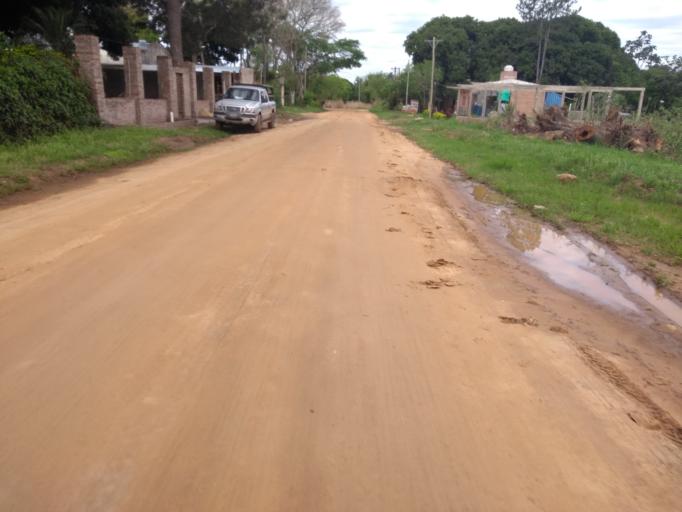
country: AR
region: Corrientes
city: San Luis del Palmar
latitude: -27.4569
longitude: -58.6555
